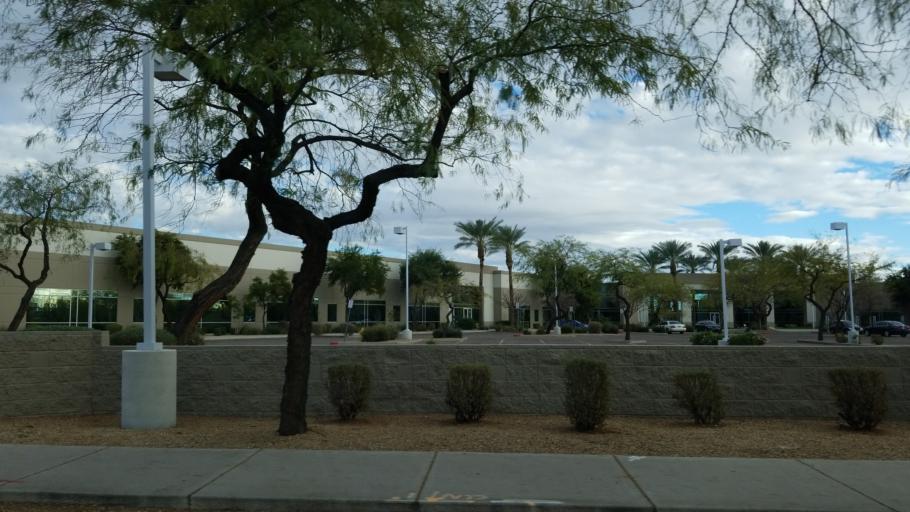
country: US
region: Arizona
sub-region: Maricopa County
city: Peoria
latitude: 33.6725
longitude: -112.1199
